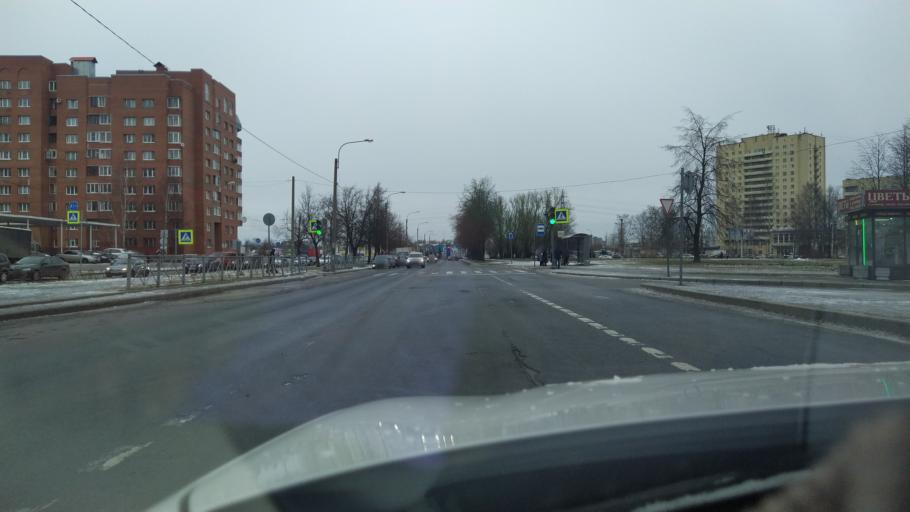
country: RU
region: St.-Petersburg
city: Grazhdanka
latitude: 60.0126
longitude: 30.4300
